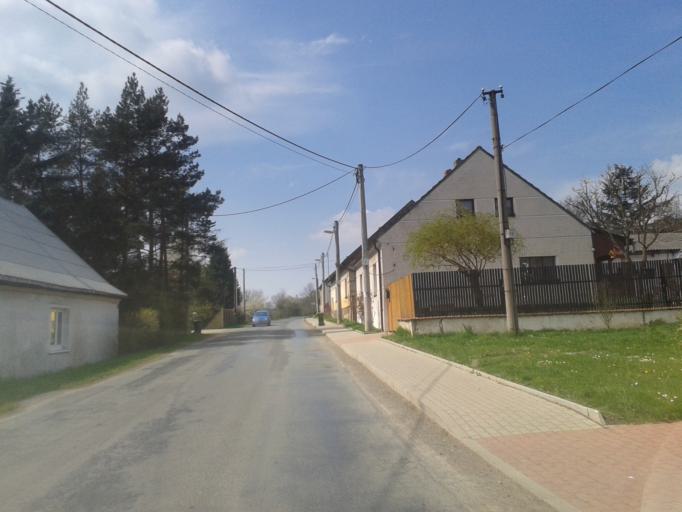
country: CZ
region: Central Bohemia
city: Chynava
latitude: 50.0112
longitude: 14.1135
